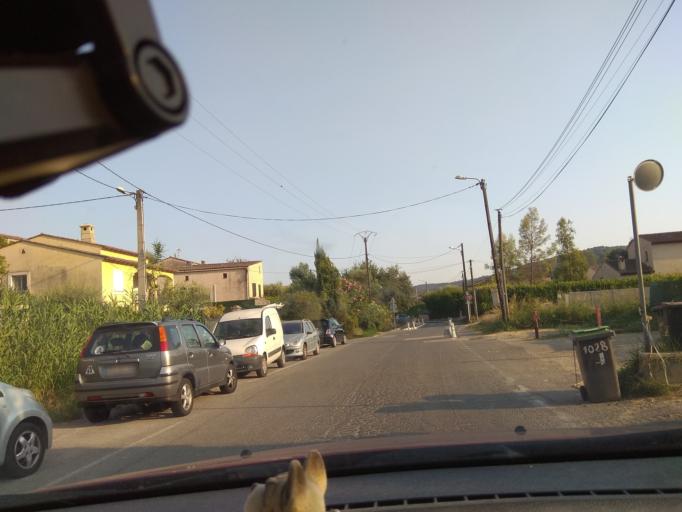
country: FR
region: Provence-Alpes-Cote d'Azur
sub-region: Departement des Alpes-Maritimes
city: La Colle-sur-Loup
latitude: 43.6793
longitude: 7.1071
